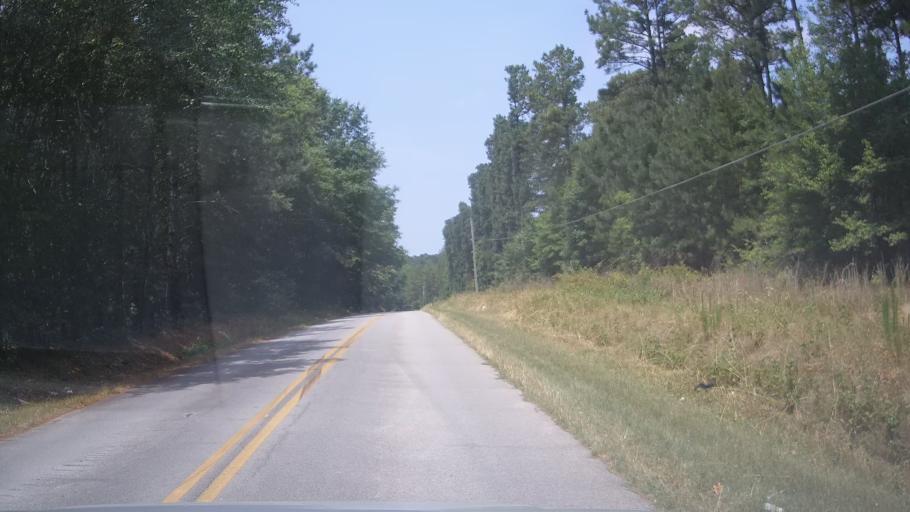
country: US
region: Georgia
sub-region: Hart County
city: Hartwell
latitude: 34.3462
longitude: -82.9035
